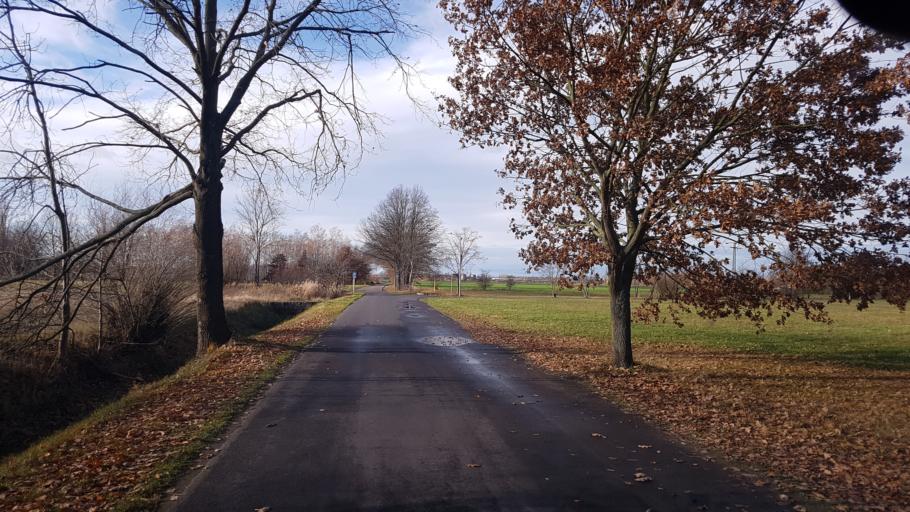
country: DE
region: Brandenburg
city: Falkenberg
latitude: 51.5926
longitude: 13.2616
